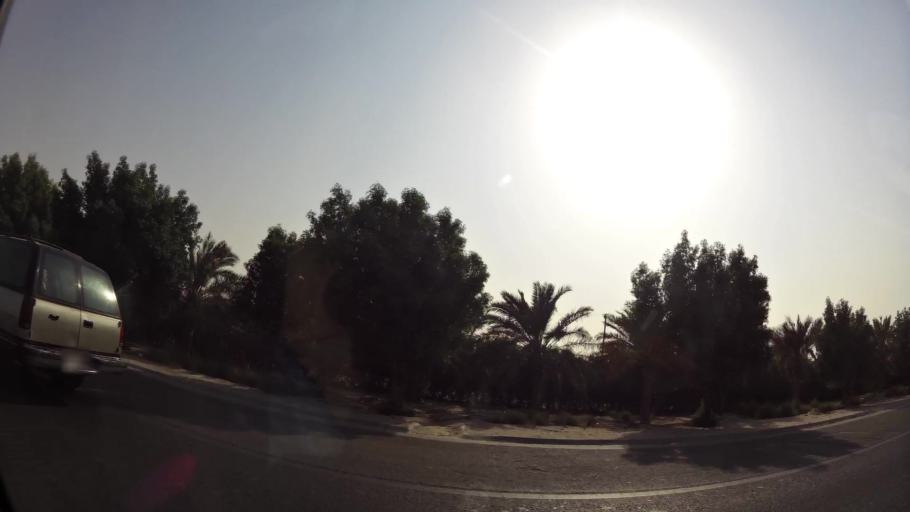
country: KW
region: Muhafazat al Jahra'
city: Al Jahra'
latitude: 29.3186
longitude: 47.7616
